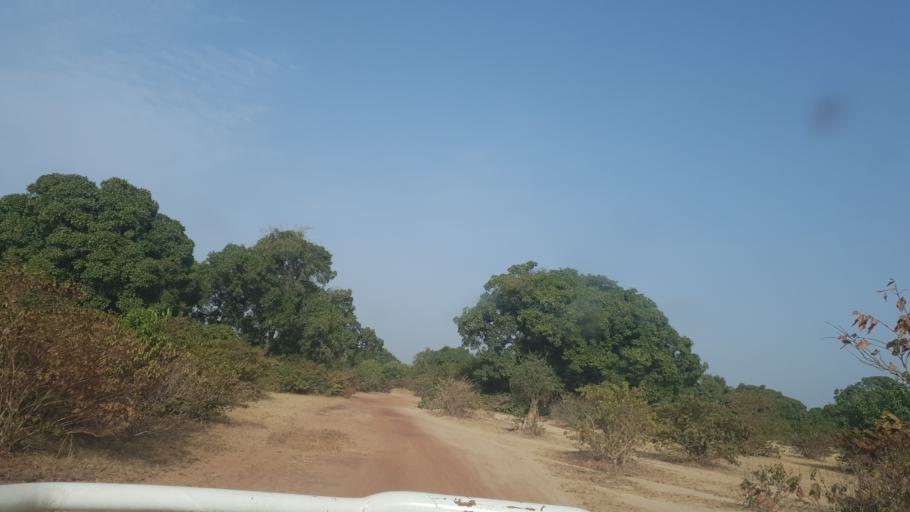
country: ML
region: Segou
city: Baroueli
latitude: 13.3607
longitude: -6.9220
